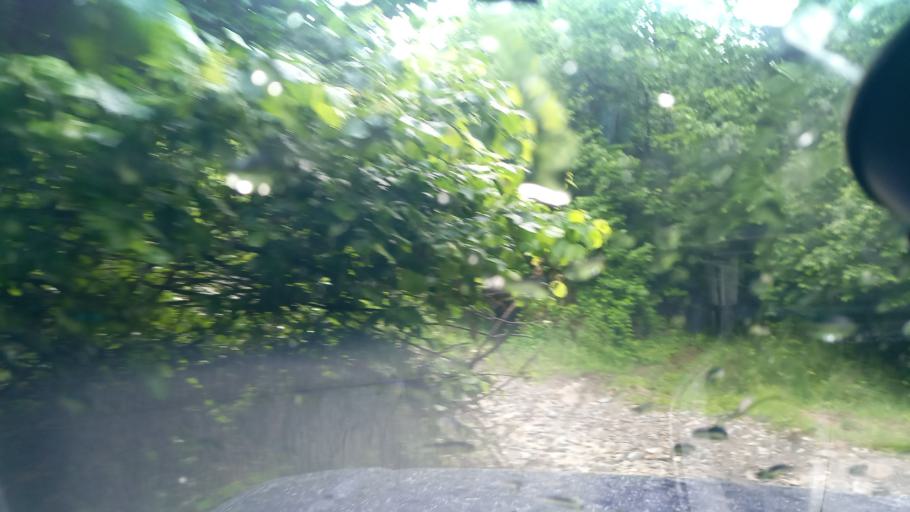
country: RU
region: Krasnodarskiy
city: Psebay
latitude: 44.0149
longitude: 40.7149
